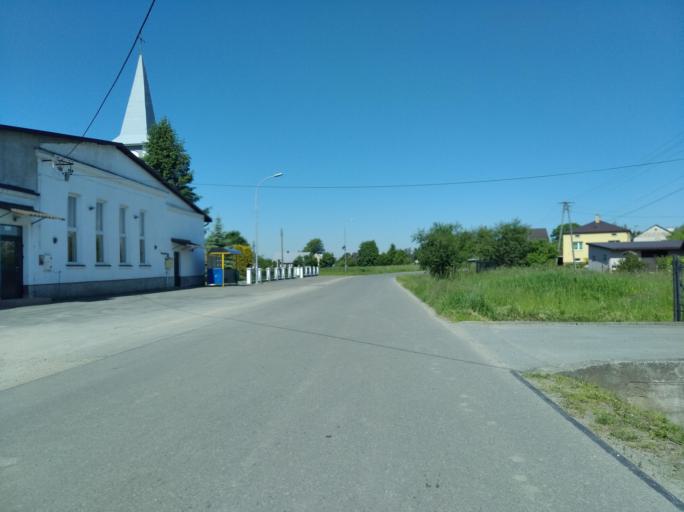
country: PL
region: Subcarpathian Voivodeship
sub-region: Krosno
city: Krosno
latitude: 49.7204
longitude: 21.7719
